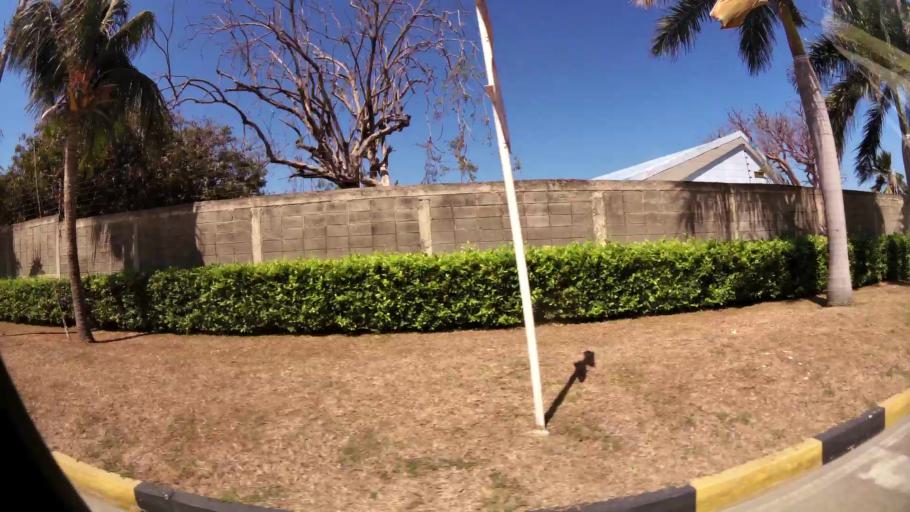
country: CO
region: Atlantico
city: Barranquilla
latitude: 11.0187
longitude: -74.8418
